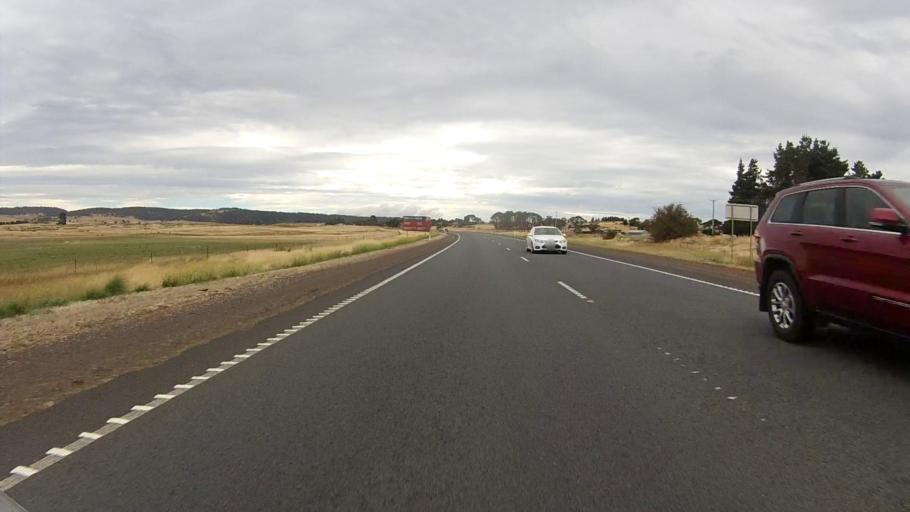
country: AU
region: Tasmania
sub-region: Brighton
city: Bridgewater
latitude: -42.3193
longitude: 147.3502
